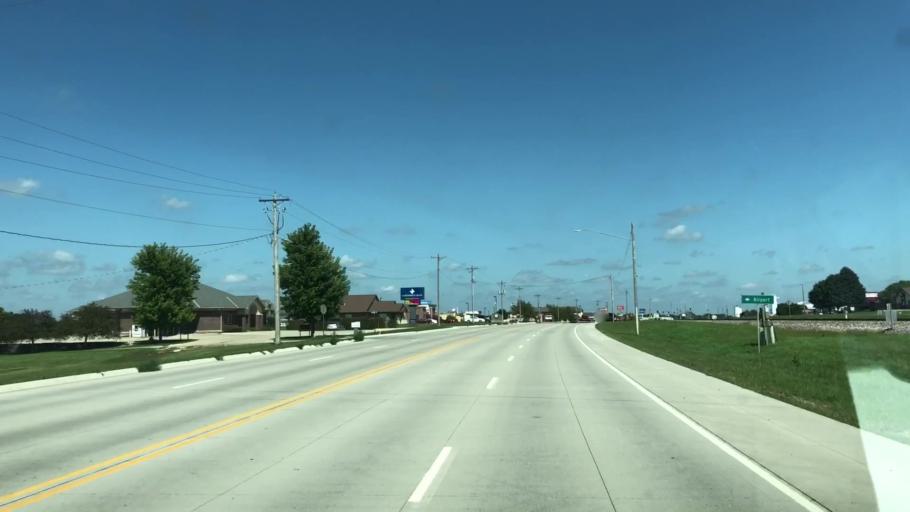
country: US
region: Iowa
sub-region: Plymouth County
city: Le Mars
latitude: 42.7752
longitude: -96.1898
